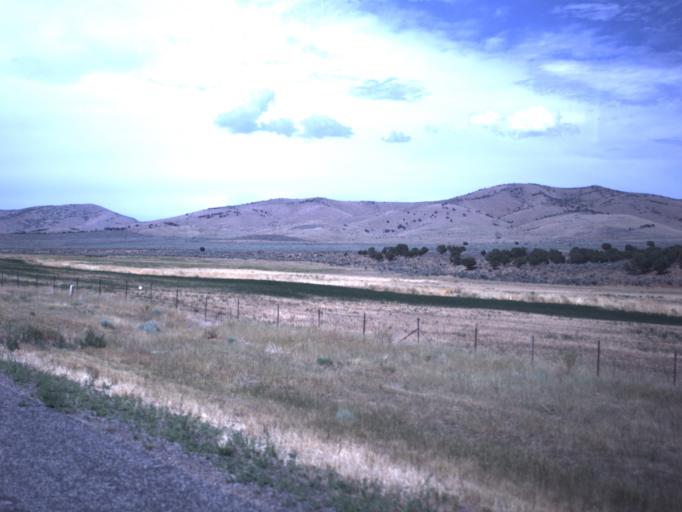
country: US
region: Utah
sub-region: Sanpete County
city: Fountain Green
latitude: 39.6409
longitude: -111.6353
